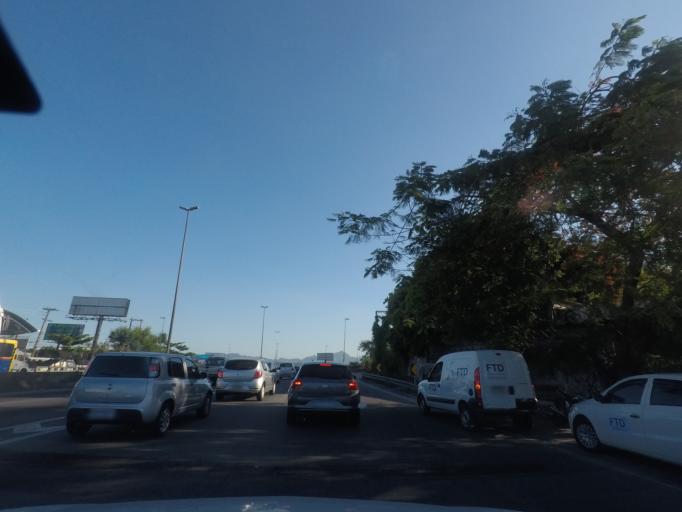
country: BR
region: Rio de Janeiro
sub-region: Duque De Caxias
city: Duque de Caxias
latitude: -22.8015
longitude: -43.2906
